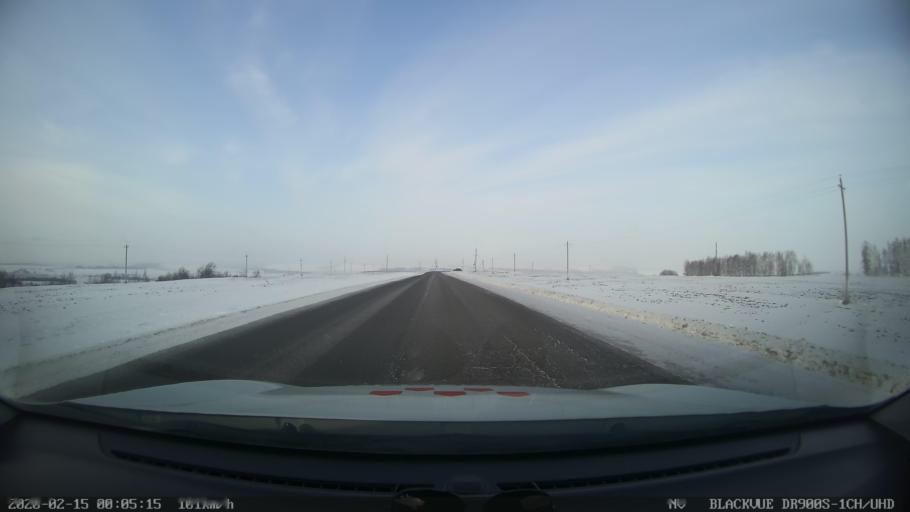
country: RU
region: Tatarstan
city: Kuybyshevskiy Zaton
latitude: 55.3931
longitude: 48.9792
